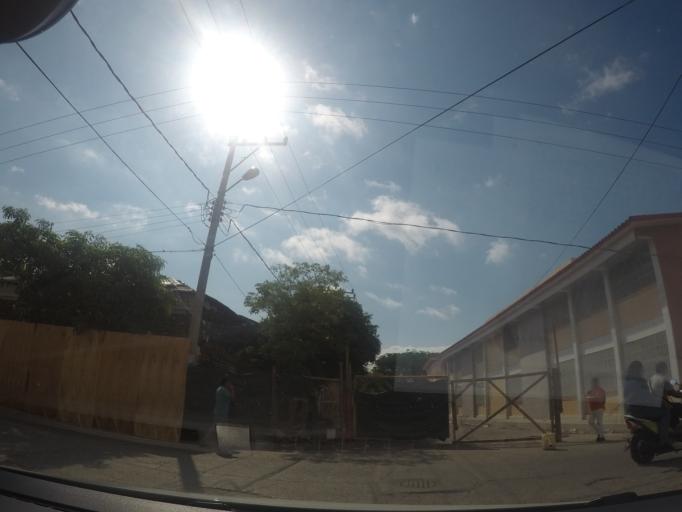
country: MX
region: Oaxaca
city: Juchitan de Zaragoza
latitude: 16.4321
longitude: -95.0240
